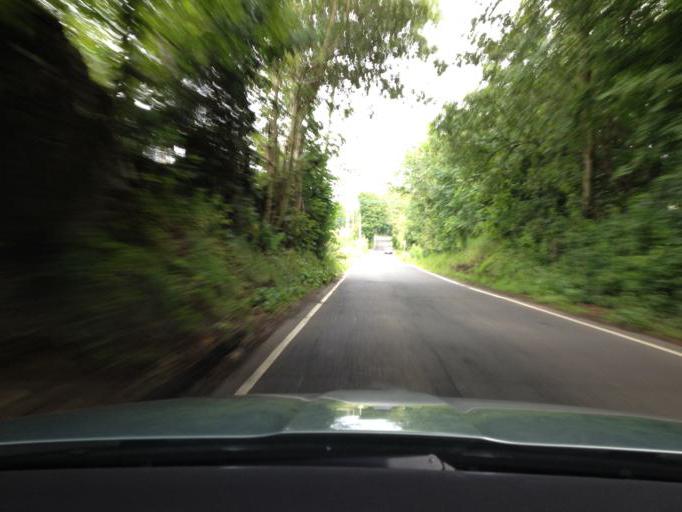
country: GB
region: Scotland
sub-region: West Lothian
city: Bathgate
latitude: 55.9311
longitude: -3.6653
